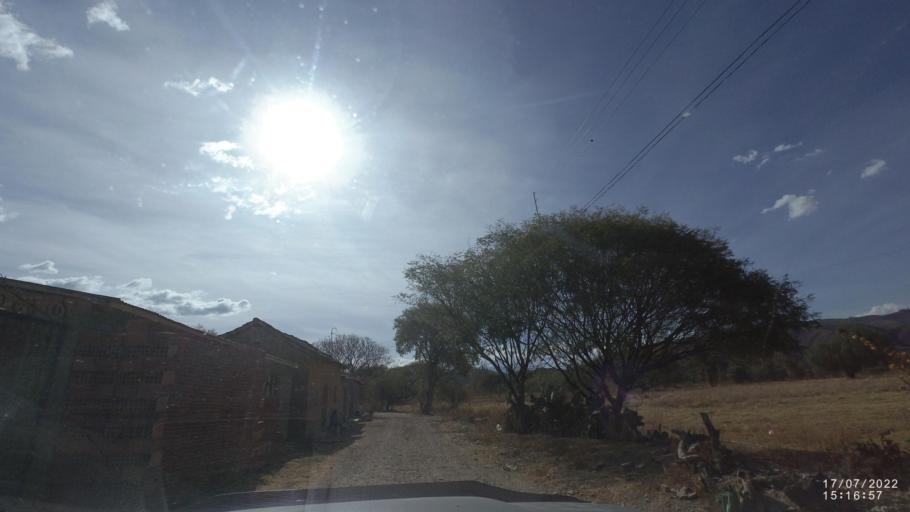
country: BO
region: Cochabamba
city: Sipe Sipe
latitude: -17.5523
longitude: -66.2661
